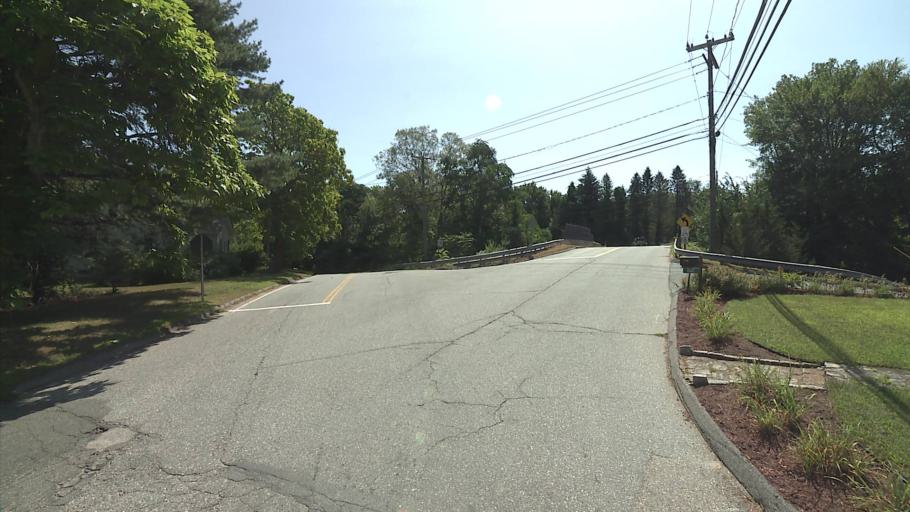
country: US
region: Connecticut
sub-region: New London County
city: Baltic
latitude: 41.6143
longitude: -72.0503
